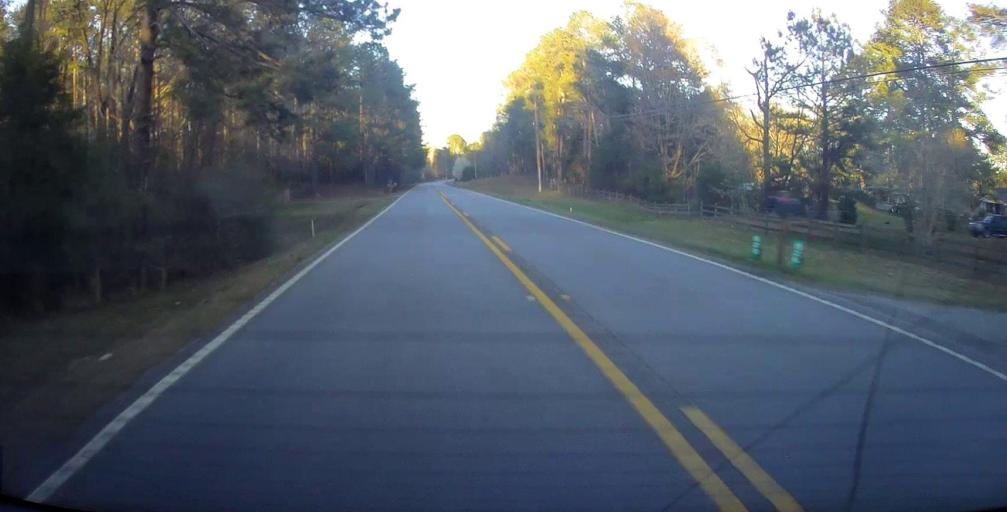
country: US
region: Alabama
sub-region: Lee County
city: Smiths Station
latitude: 32.6359
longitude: -85.0307
